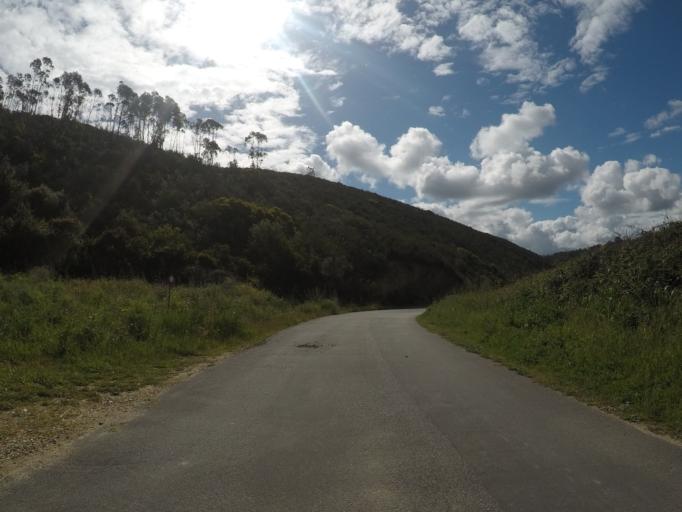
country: PT
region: Beja
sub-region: Odemira
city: Sao Teotonio
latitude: 37.4379
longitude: -8.7879
